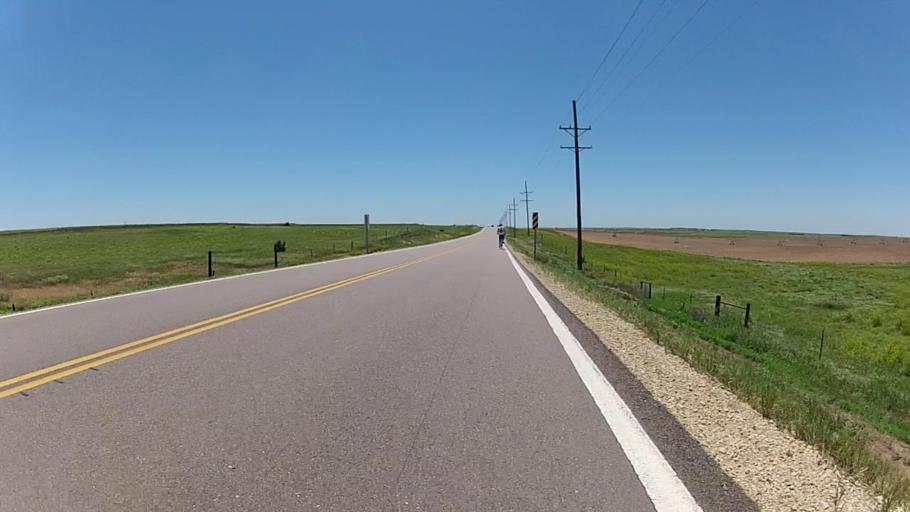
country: US
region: Kansas
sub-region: Kiowa County
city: Greensburg
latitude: 37.5189
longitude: -99.3206
